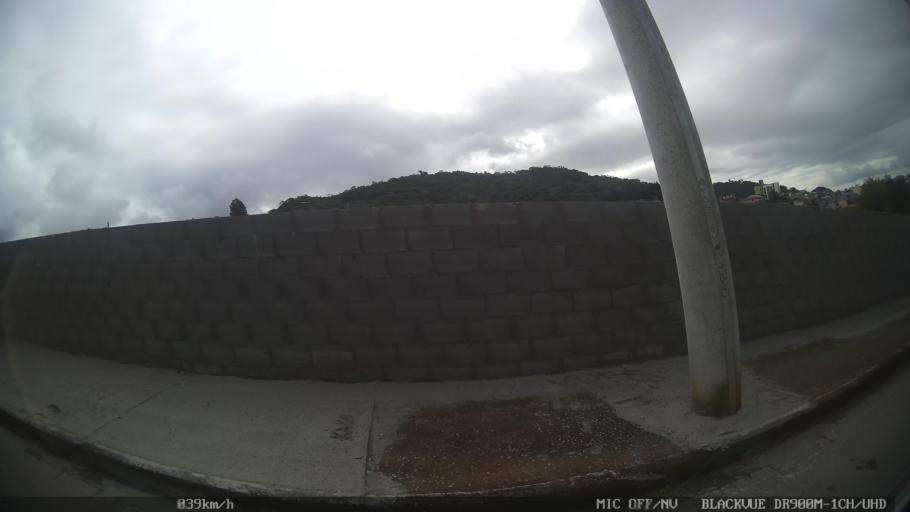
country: BR
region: Santa Catarina
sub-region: Biguacu
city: Biguacu
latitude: -27.5275
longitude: -48.6490
